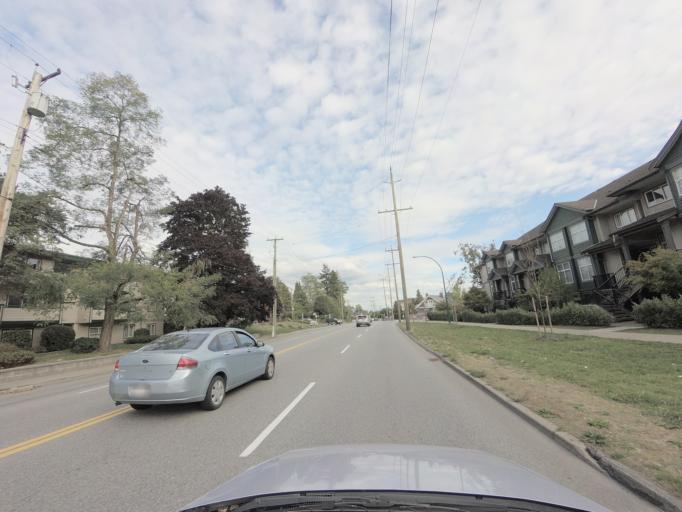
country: CA
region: British Columbia
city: New Westminster
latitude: 49.2171
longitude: -122.9448
